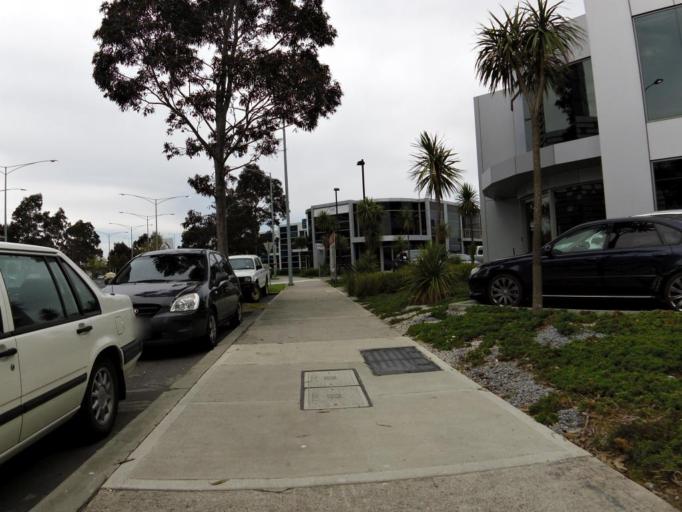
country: AU
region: Victoria
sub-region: Melbourne
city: Docklands
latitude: -37.8245
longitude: 144.9425
